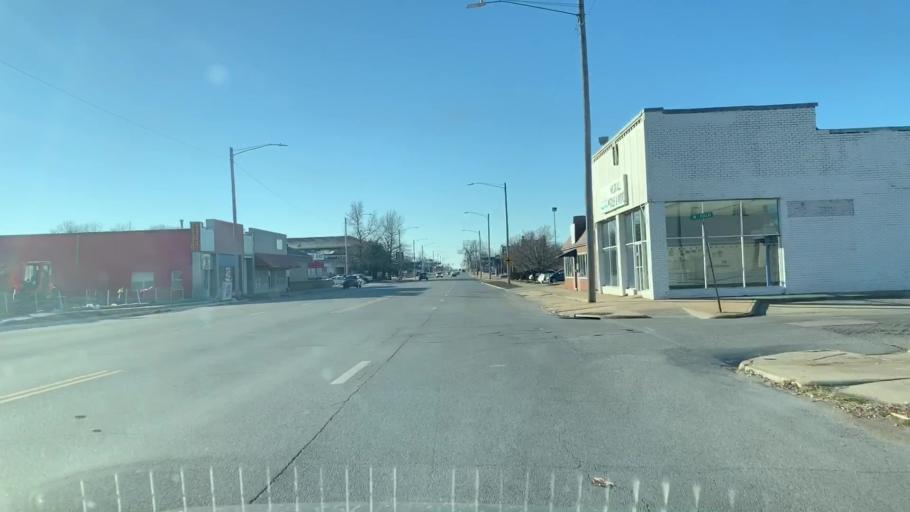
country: US
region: Kansas
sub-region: Crawford County
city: Pittsburg
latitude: 37.4065
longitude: -94.7050
